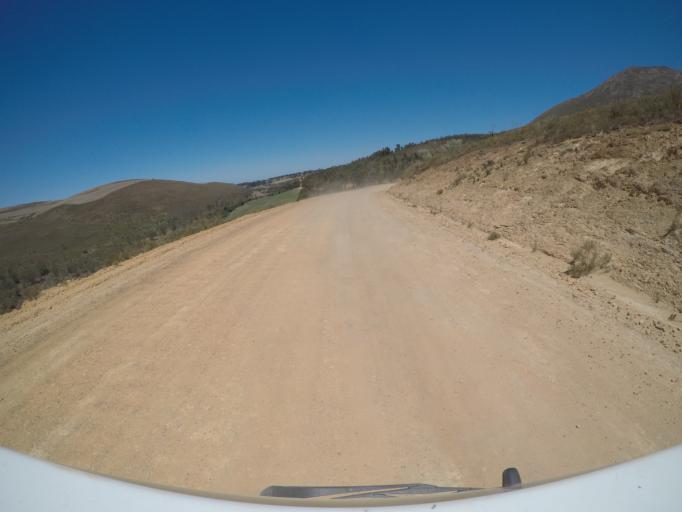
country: ZA
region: Western Cape
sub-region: Overberg District Municipality
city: Grabouw
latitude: -34.2062
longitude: 19.2159
